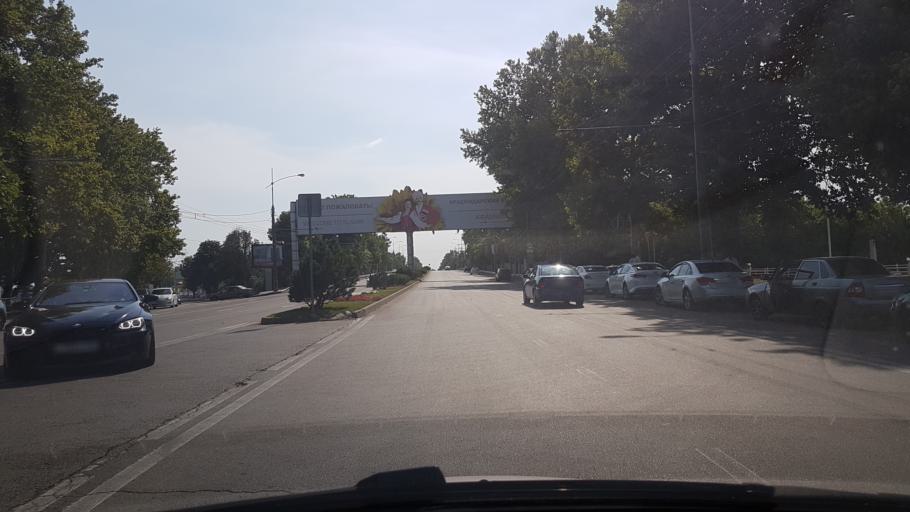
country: RU
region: Krasnodarskiy
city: Pashkovskiy
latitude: 45.0328
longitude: 39.1347
